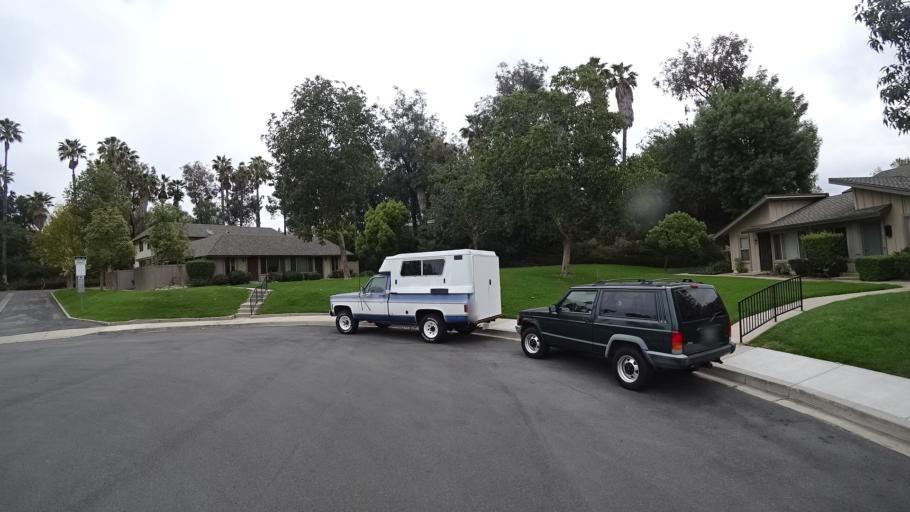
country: US
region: California
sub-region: Ventura County
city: Thousand Oaks
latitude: 34.2096
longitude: -118.8476
